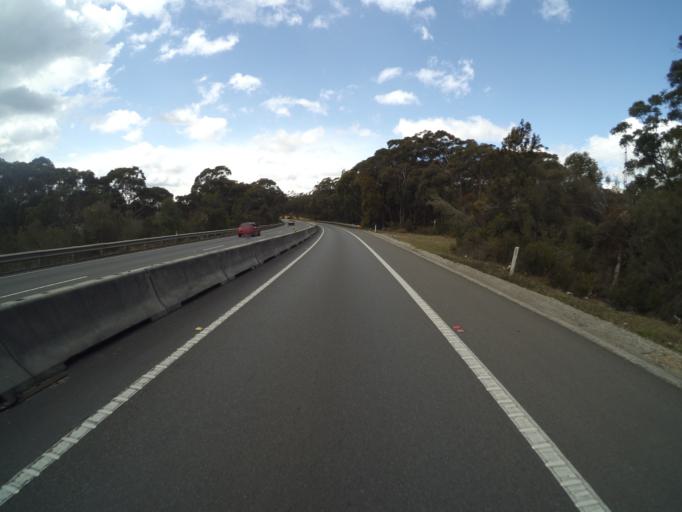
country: AU
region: New South Wales
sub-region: Wollongong
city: Mount Keira
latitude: -34.3474
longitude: 150.7978
